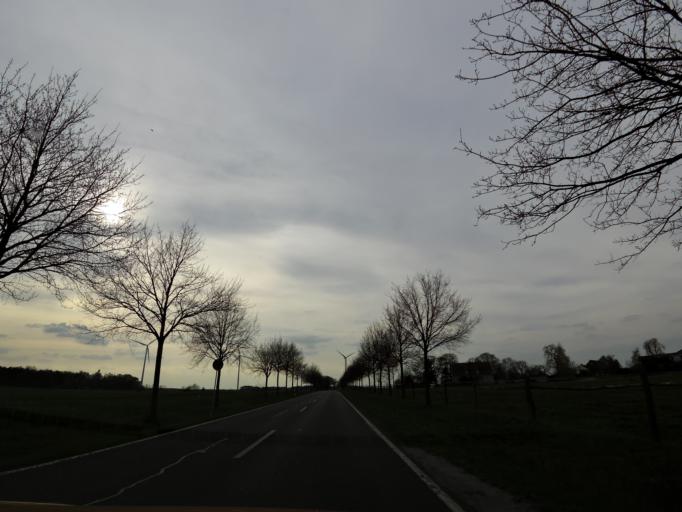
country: DE
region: Brandenburg
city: Bestensee
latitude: 52.2446
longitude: 13.6012
